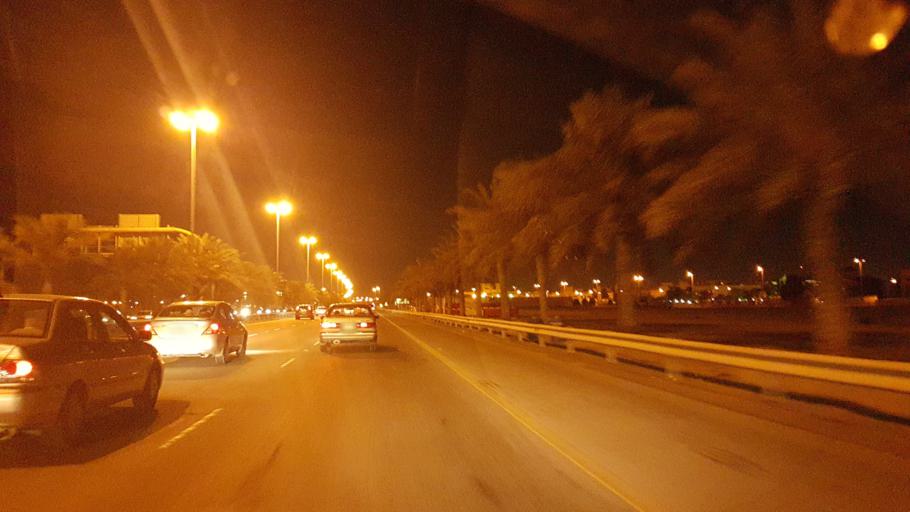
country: BH
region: Muharraq
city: Al Hadd
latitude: 26.2503
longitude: 50.6591
